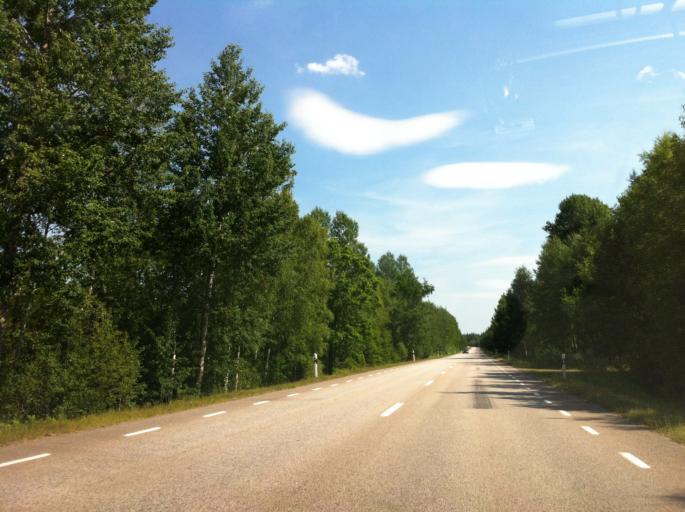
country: SE
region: Kalmar
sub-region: Nybro Kommun
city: Nybro
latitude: 56.8319
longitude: 15.7423
